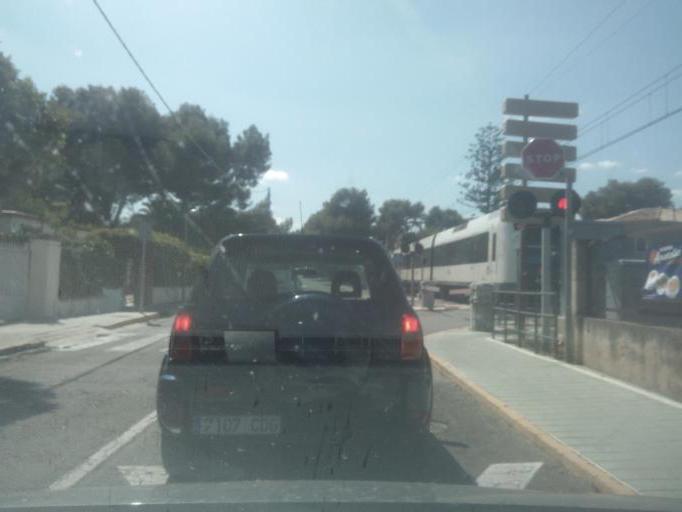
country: ES
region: Valencia
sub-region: Provincia de Valencia
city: Manises
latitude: 39.5293
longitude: -0.4889
